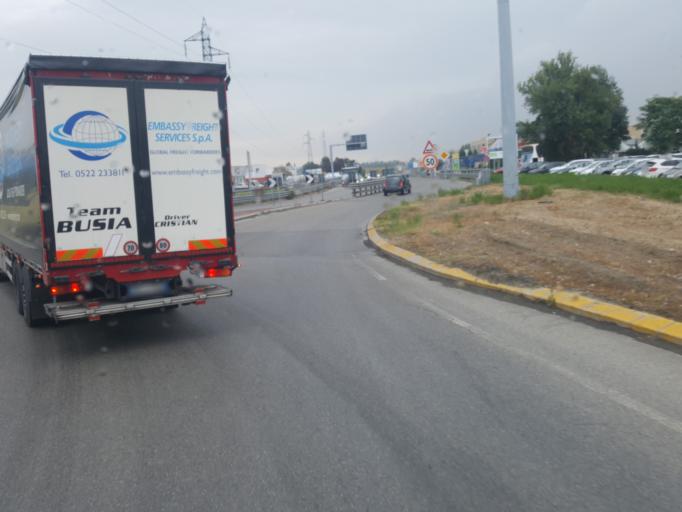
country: IT
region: Emilia-Romagna
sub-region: Provincia di Modena
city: Fiorano
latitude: 44.5522
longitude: 10.8158
